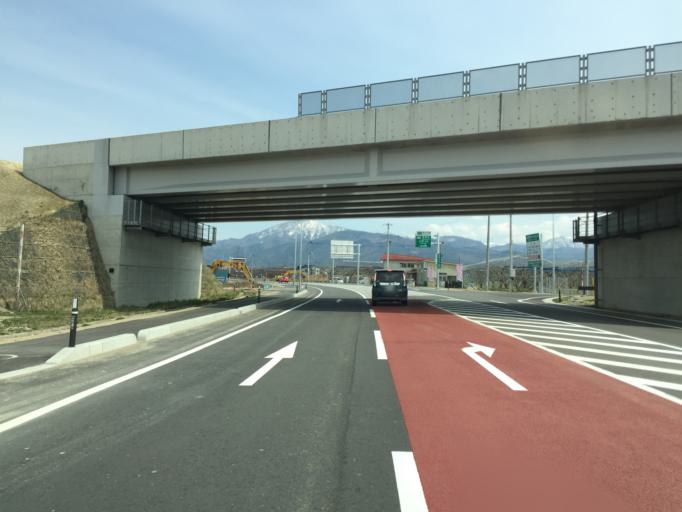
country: JP
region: Yamagata
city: Higashine
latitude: 38.4471
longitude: 140.3535
